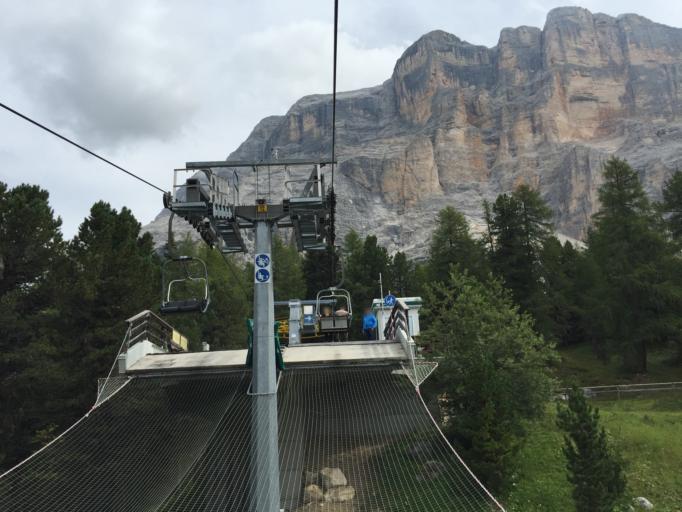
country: IT
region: Trentino-Alto Adige
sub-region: Bolzano
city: Badia
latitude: 46.6146
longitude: 11.9362
